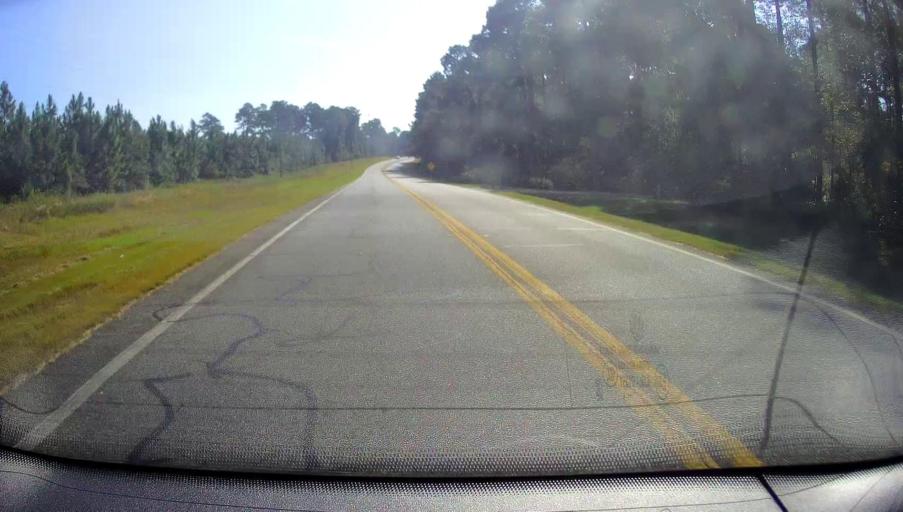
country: US
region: Georgia
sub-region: Bleckley County
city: Cochran
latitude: 32.3757
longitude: -83.3400
